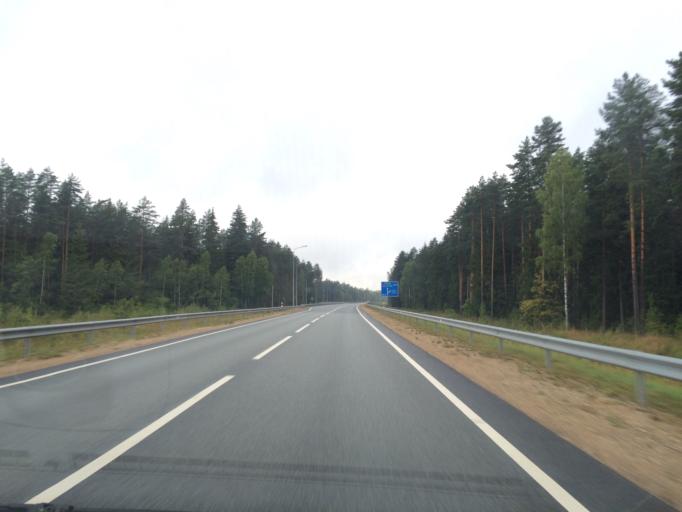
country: LV
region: Ogre
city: Ogre
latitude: 56.8413
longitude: 24.6867
